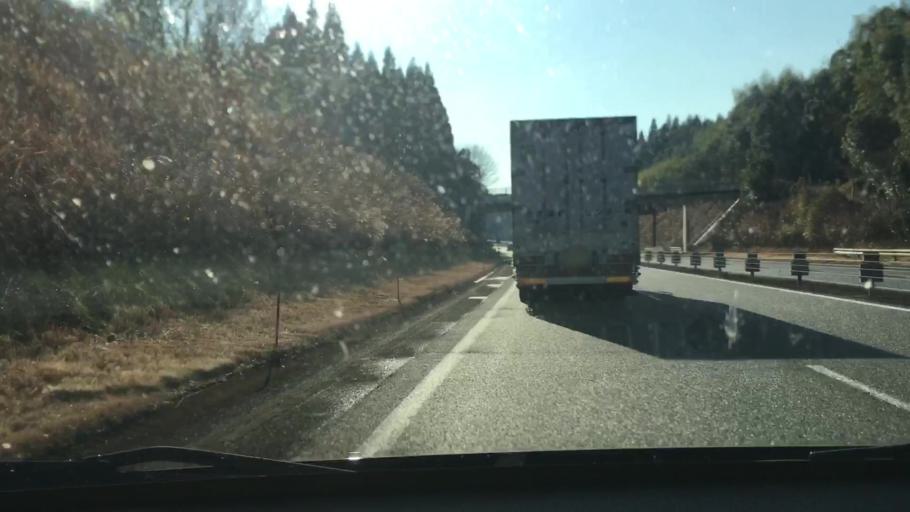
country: JP
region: Kagoshima
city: Okuchi-shinohara
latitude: 31.9419
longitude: 130.7150
